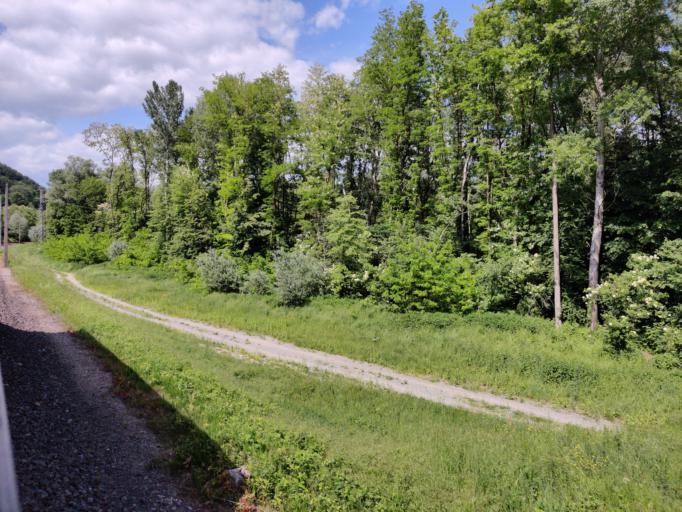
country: AT
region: Styria
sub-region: Politischer Bezirk Leibnitz
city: Stocking
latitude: 46.8625
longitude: 15.5306
